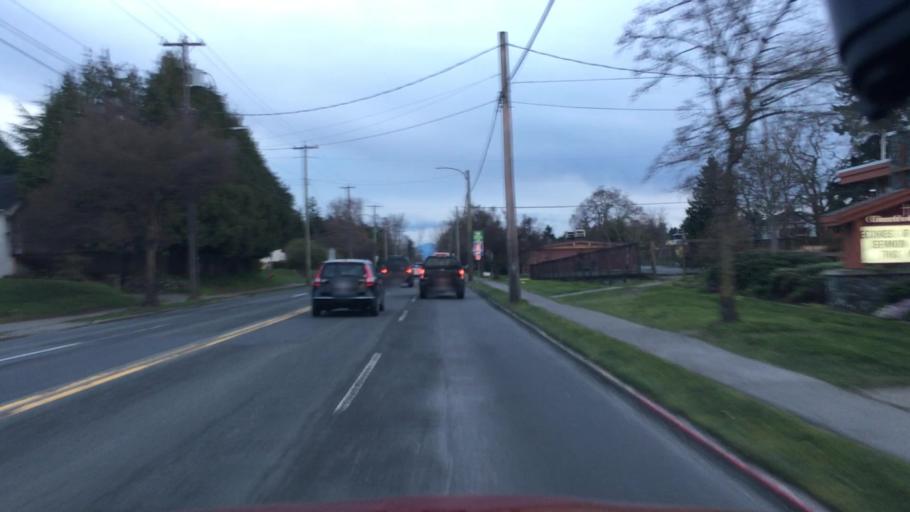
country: CA
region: British Columbia
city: Oak Bay
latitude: 48.4558
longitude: -123.3332
